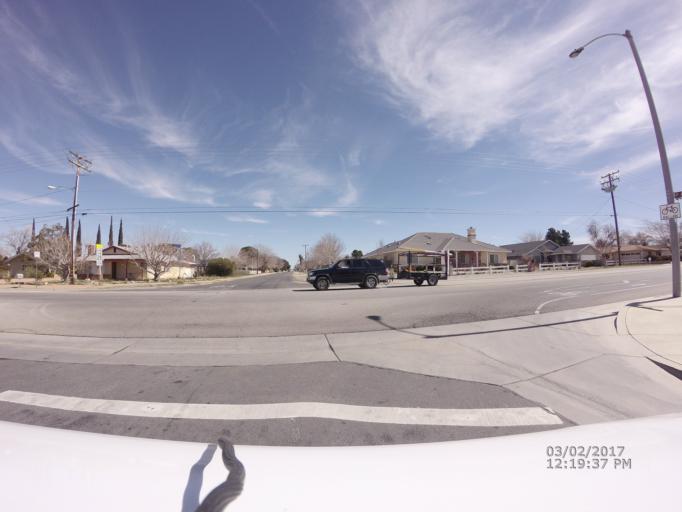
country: US
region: California
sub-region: Los Angeles County
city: Quartz Hill
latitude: 34.6492
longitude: -118.2275
